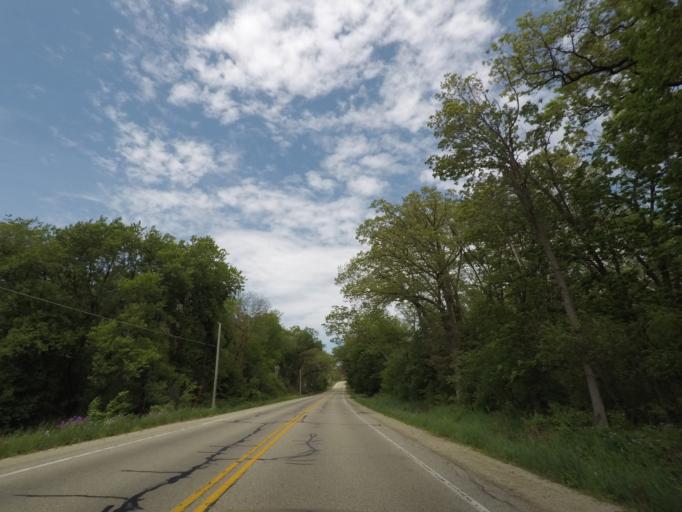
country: US
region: Wisconsin
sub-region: Rock County
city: Orfordville
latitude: 42.6396
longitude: -89.2758
